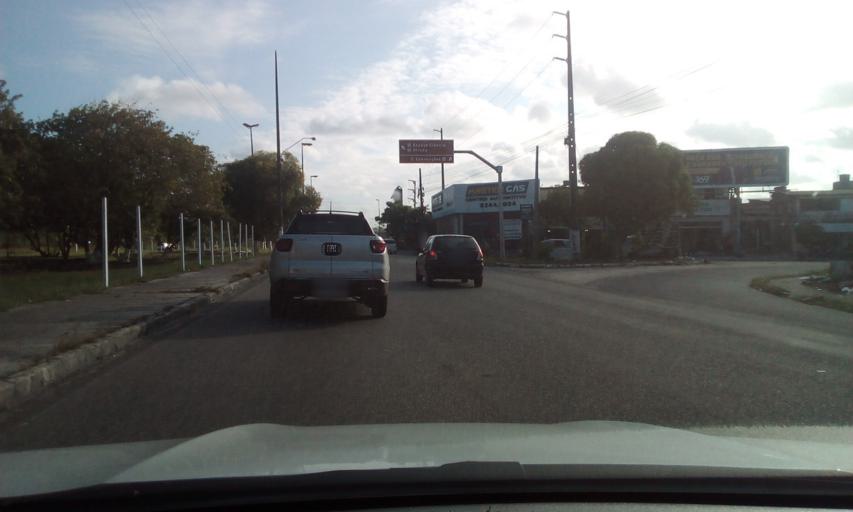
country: BR
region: Pernambuco
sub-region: Olinda
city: Olinda
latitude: -8.0299
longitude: -34.8665
